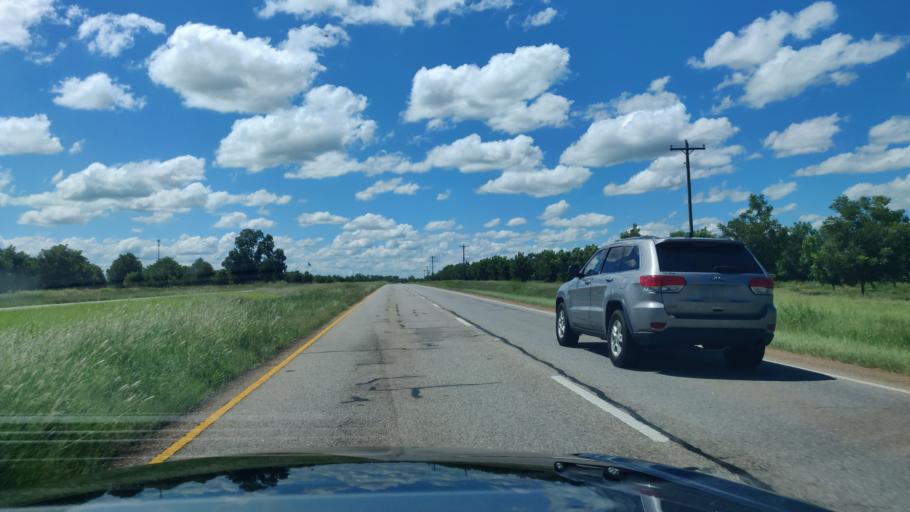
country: US
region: Georgia
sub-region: Webster County
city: Preston
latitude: 31.9358
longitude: -84.5646
